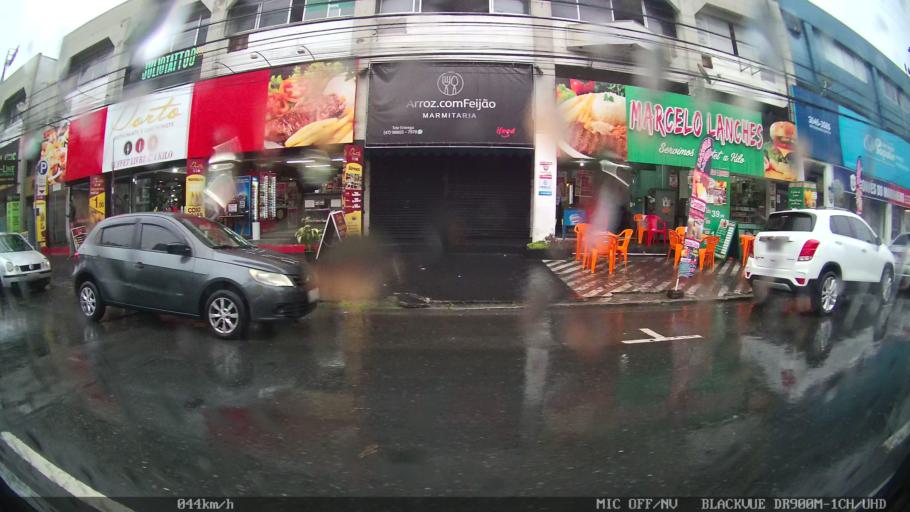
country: BR
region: Santa Catarina
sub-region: Itajai
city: Itajai
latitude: -26.9075
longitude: -48.6590
